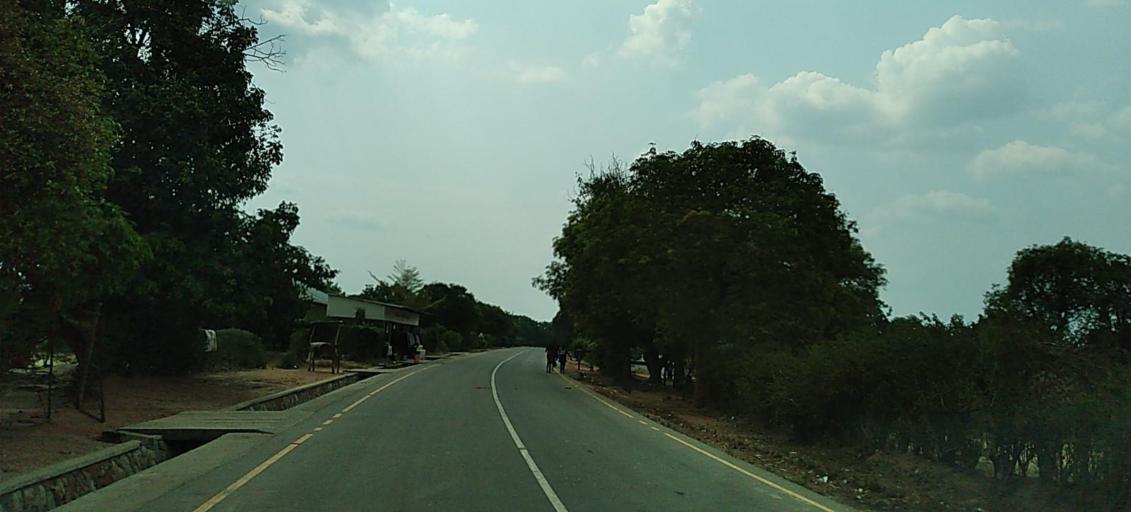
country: ZM
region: Copperbelt
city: Kalulushi
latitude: -12.8551
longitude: 28.1307
